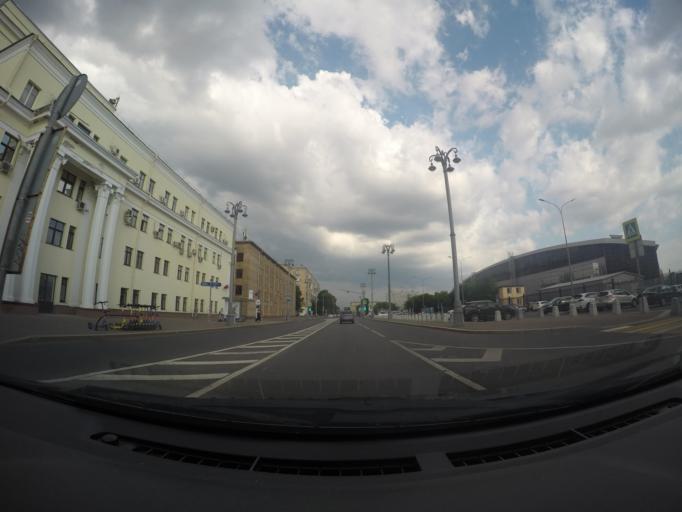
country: RU
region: Moscow
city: Sviblovo
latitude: 55.8332
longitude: 37.6375
